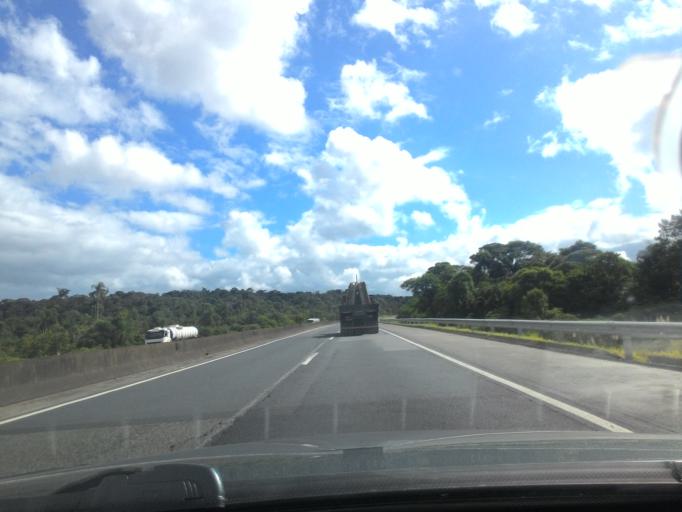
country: BR
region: Sao Paulo
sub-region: Cajati
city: Cajati
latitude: -24.9199
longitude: -48.2589
